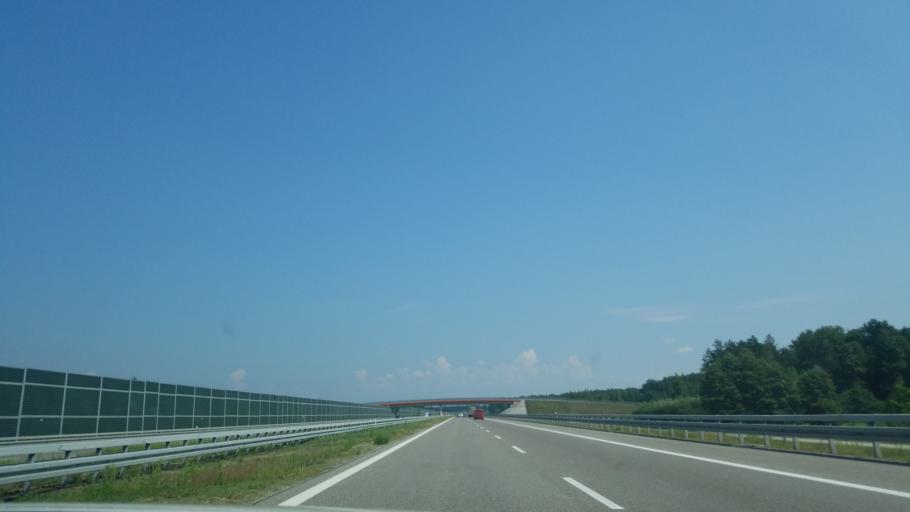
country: PL
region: Subcarpathian Voivodeship
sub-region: Powiat rzeszowski
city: Trzciana
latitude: 50.1148
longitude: 21.7720
